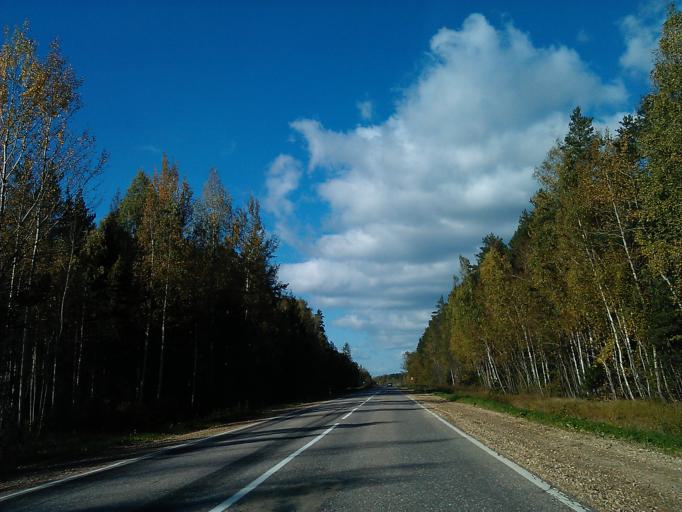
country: LV
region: Livani
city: Livani
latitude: 56.1904
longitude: 26.2960
